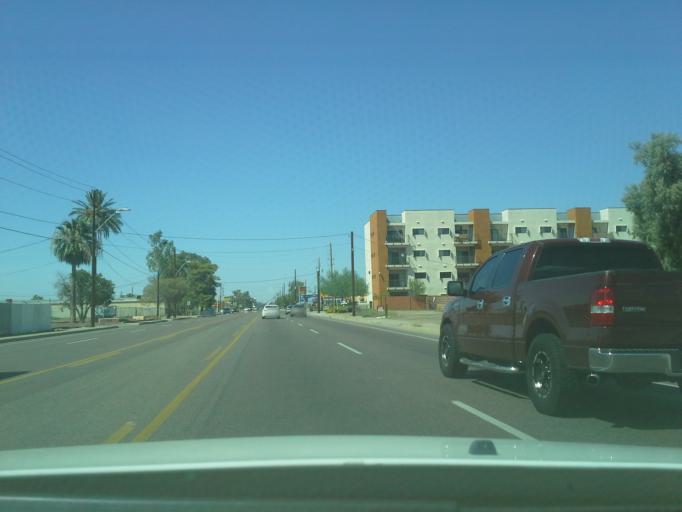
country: US
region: Arizona
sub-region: Maricopa County
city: Phoenix
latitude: 33.4085
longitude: -112.0646
